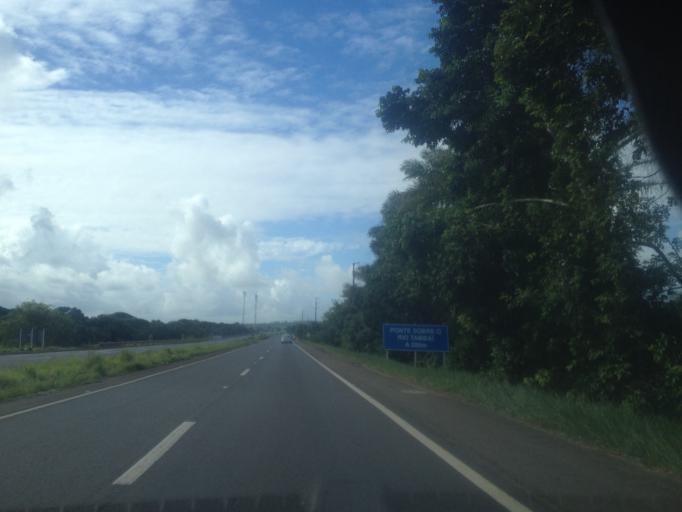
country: BR
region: Bahia
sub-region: Mata De Sao Joao
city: Mata de Sao Joao
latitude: -12.6120
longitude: -38.0529
